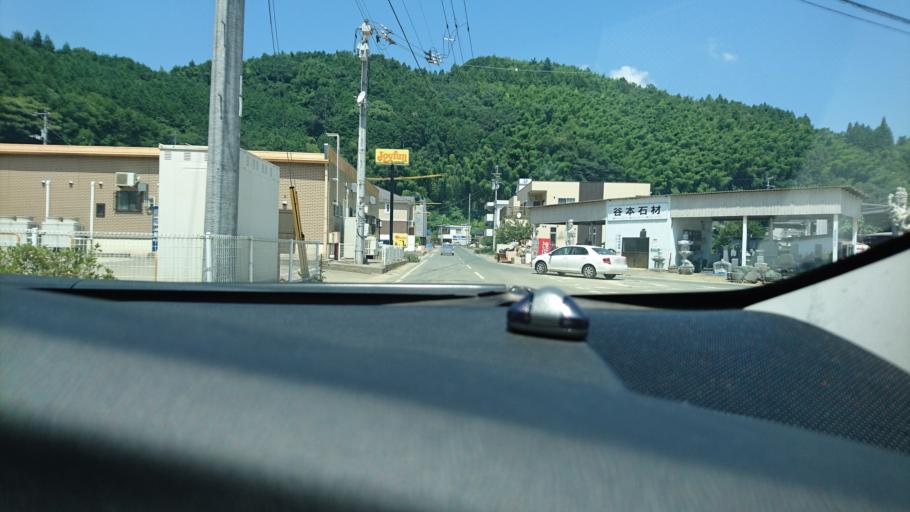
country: JP
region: Ehime
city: Ozu
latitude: 33.4991
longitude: 132.5477
